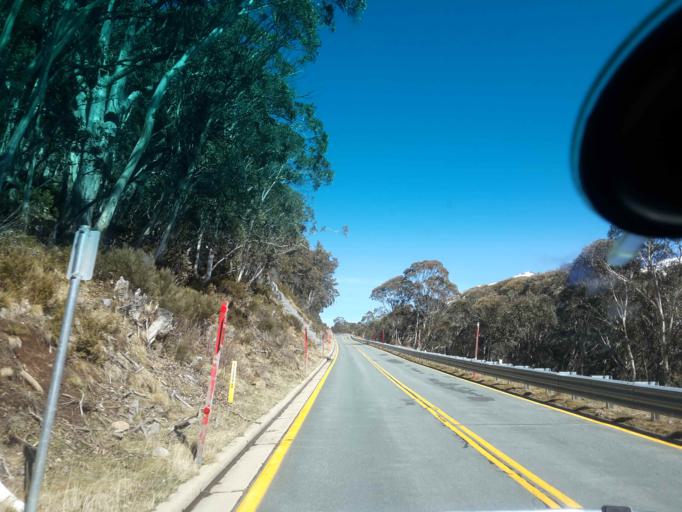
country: AU
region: New South Wales
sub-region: Snowy River
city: Jindabyne
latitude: -36.5019
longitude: 148.3140
